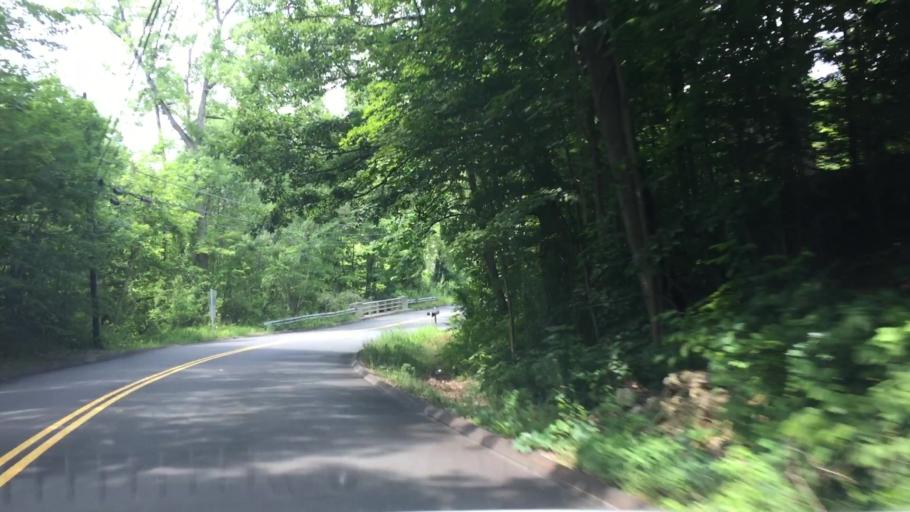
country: US
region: Massachusetts
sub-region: Berkshire County
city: Lee
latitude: 42.2941
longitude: -73.2254
